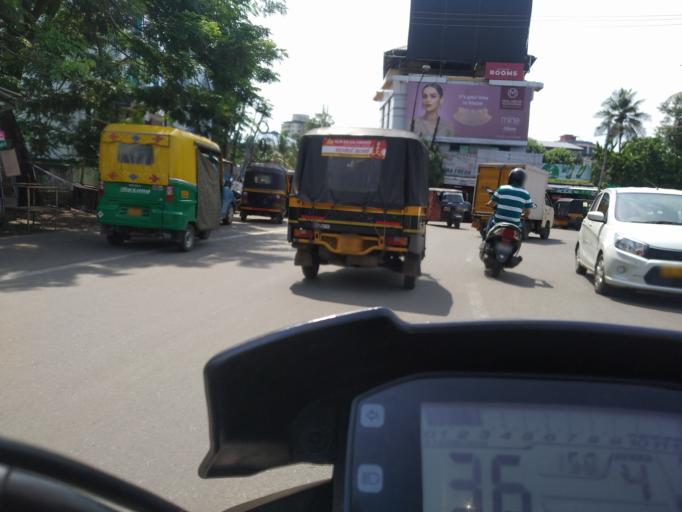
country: IN
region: Kerala
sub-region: Ernakulam
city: Cochin
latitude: 9.9781
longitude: 76.2878
